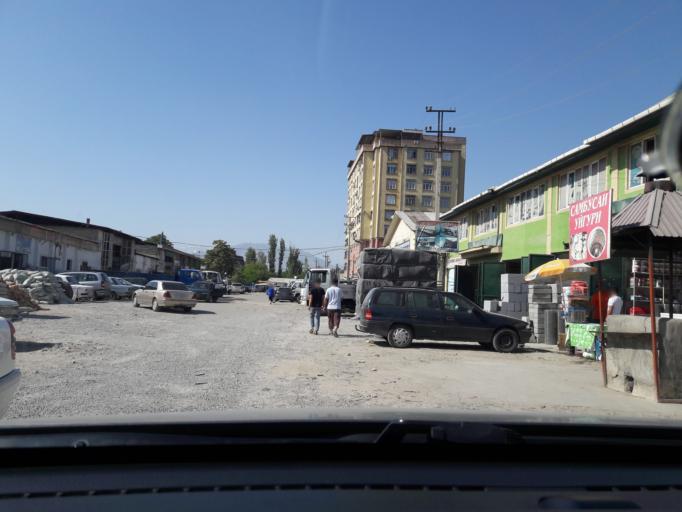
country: TJ
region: Dushanbe
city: Dushanbe
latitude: 38.5471
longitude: 68.7554
